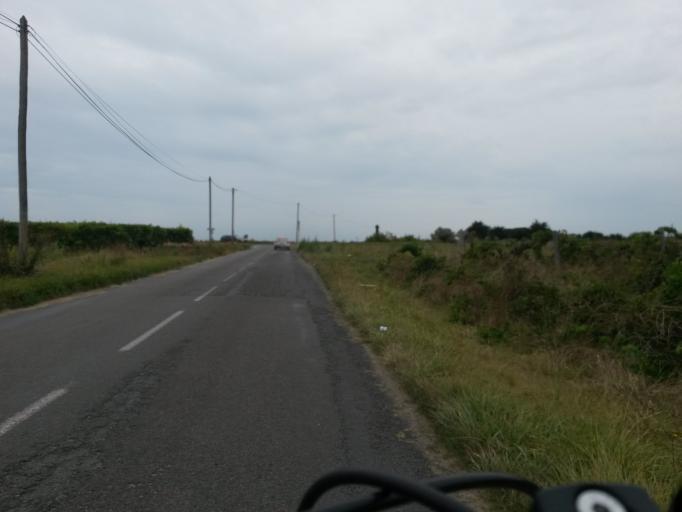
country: FR
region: Poitou-Charentes
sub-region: Departement de la Charente-Maritime
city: Dolus-d'Oleron
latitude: 45.9351
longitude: -1.3370
